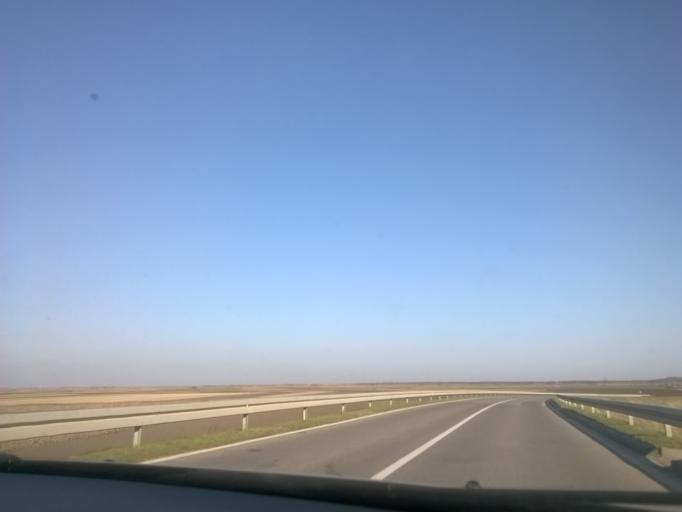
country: RS
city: Uljma
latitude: 45.0537
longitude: 21.1687
